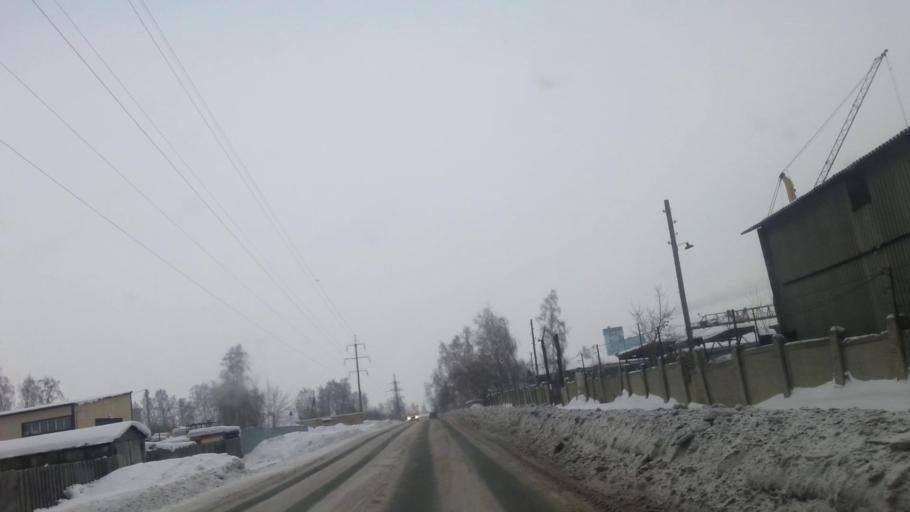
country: RU
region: Altai Krai
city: Novosilikatnyy
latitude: 53.3122
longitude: 83.6183
